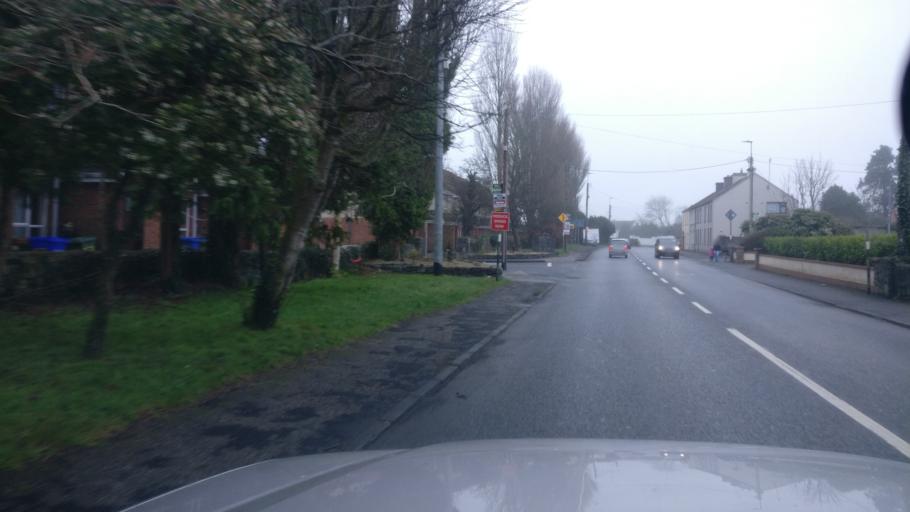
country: IE
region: Connaught
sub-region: County Galway
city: Gort
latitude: 53.0718
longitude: -8.8240
